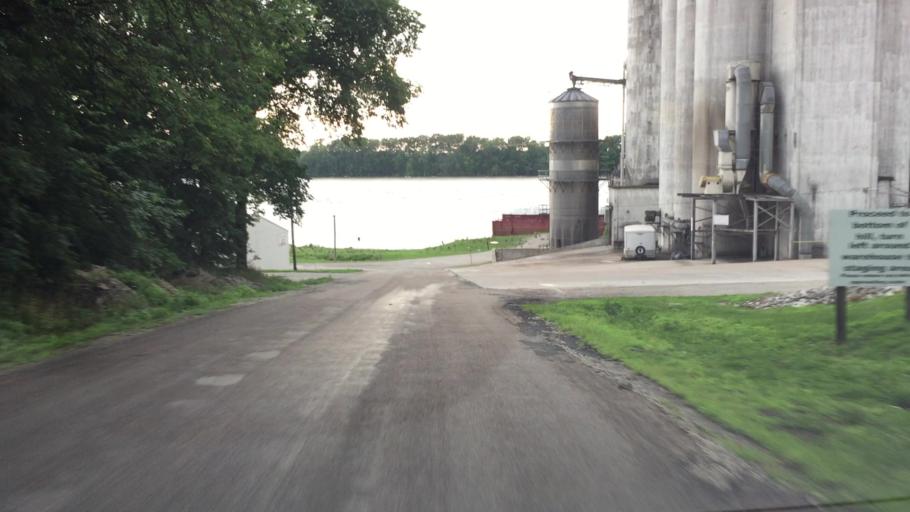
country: US
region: Illinois
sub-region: Hancock County
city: Warsaw
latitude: 40.3612
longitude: -91.4407
